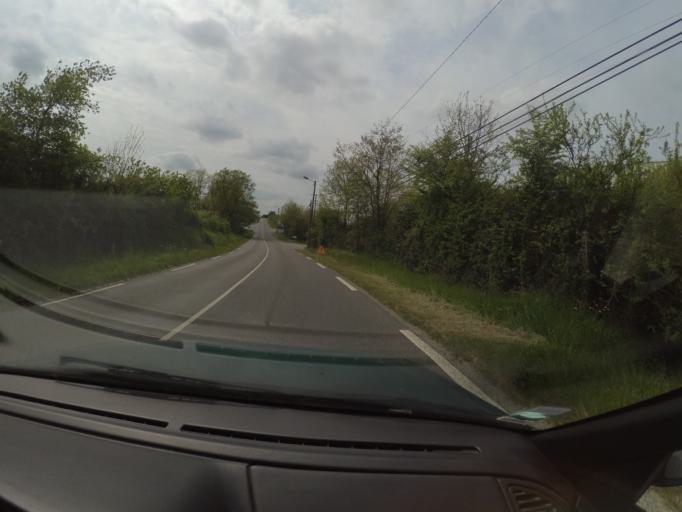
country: FR
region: Pays de la Loire
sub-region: Departement de la Loire-Atlantique
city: Gorges
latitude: 47.1025
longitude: -1.3117
